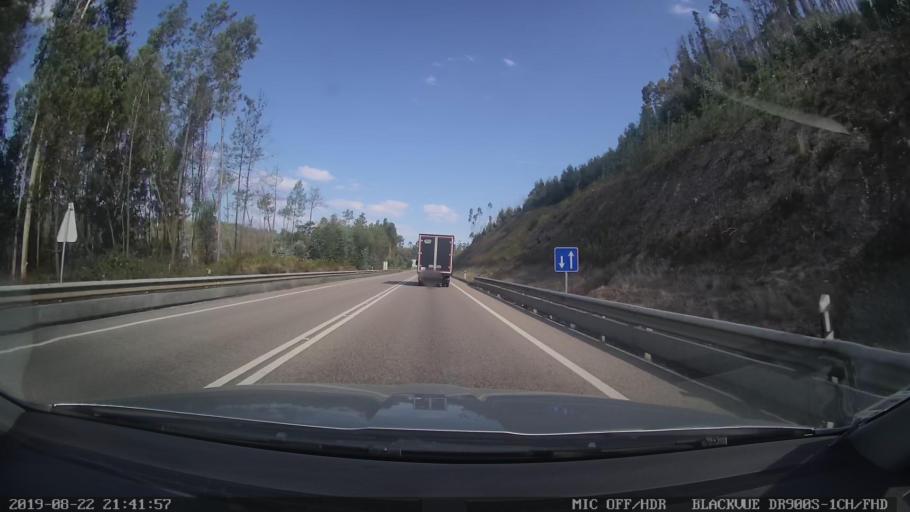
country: PT
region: Leiria
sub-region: Figueiro Dos Vinhos
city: Figueiro dos Vinhos
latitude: 39.9286
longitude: -8.3338
